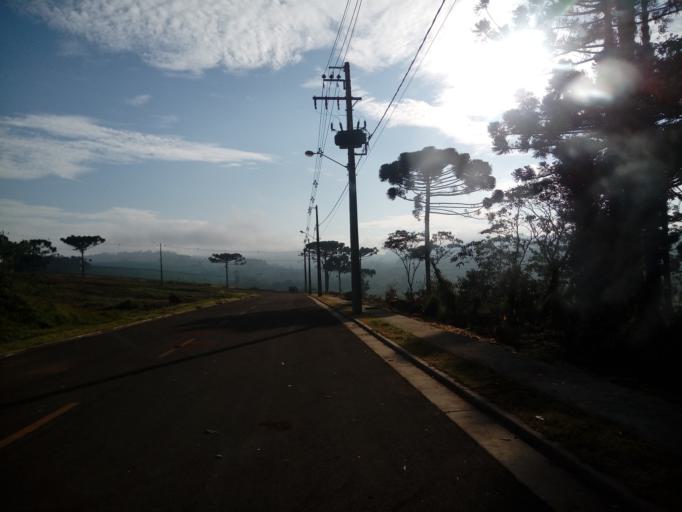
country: BR
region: Santa Catarina
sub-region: Chapeco
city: Chapeco
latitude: -27.0911
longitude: -52.7079
